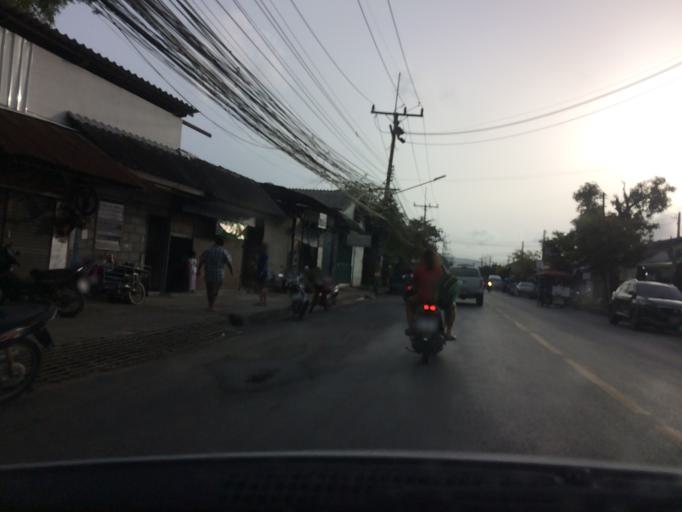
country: TH
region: Phuket
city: Ban Talat Yai
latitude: 7.8815
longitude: 98.4025
